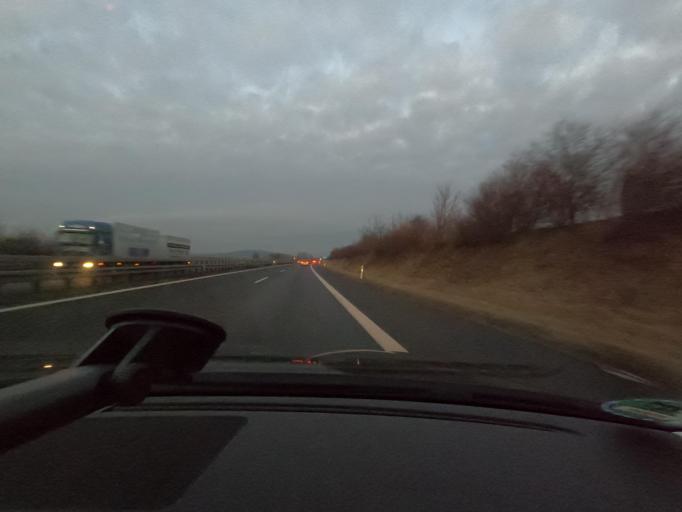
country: DE
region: Bavaria
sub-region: Upper Franconia
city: Bad Staffelstein
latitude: 50.1173
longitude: 11.0195
